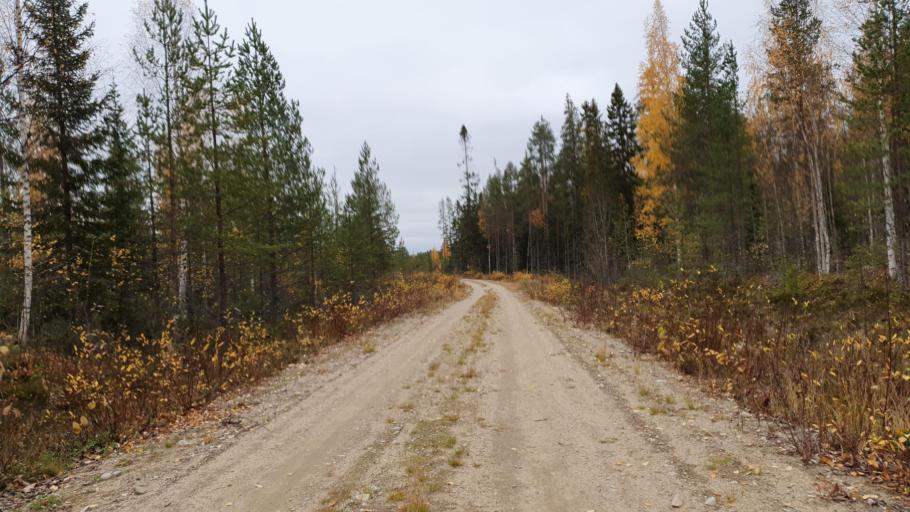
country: FI
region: Kainuu
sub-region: Kehys-Kainuu
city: Kuhmo
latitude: 64.4412
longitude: 29.6179
